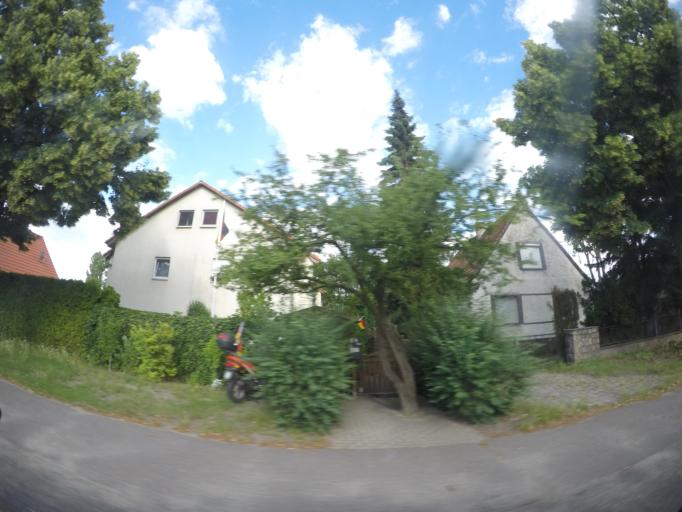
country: DE
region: Berlin
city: Karlshorst
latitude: 52.4799
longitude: 13.5598
